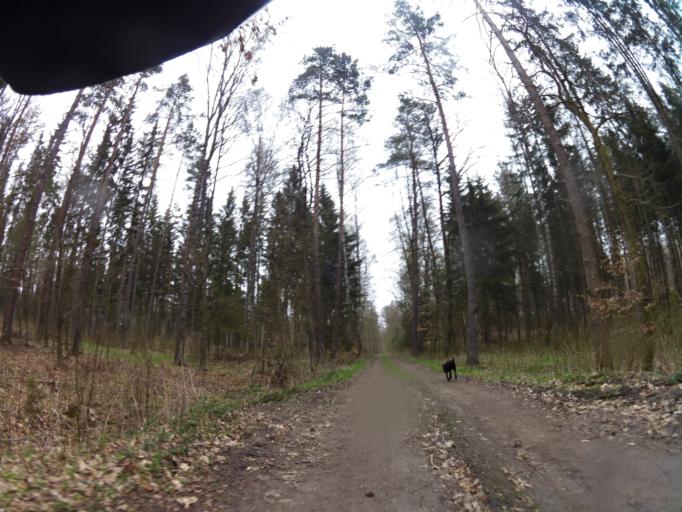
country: PL
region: West Pomeranian Voivodeship
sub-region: Powiat koszalinski
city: Bobolice
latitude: 53.9835
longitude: 16.6459
